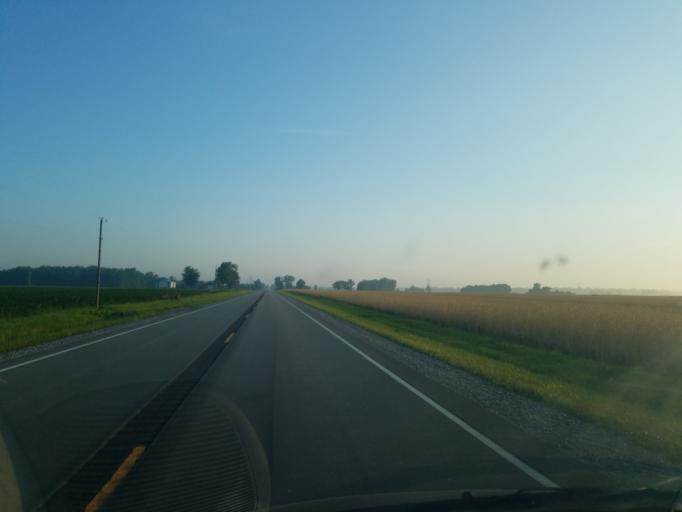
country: US
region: Indiana
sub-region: Allen County
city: Harlan
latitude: 41.2132
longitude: -84.8652
